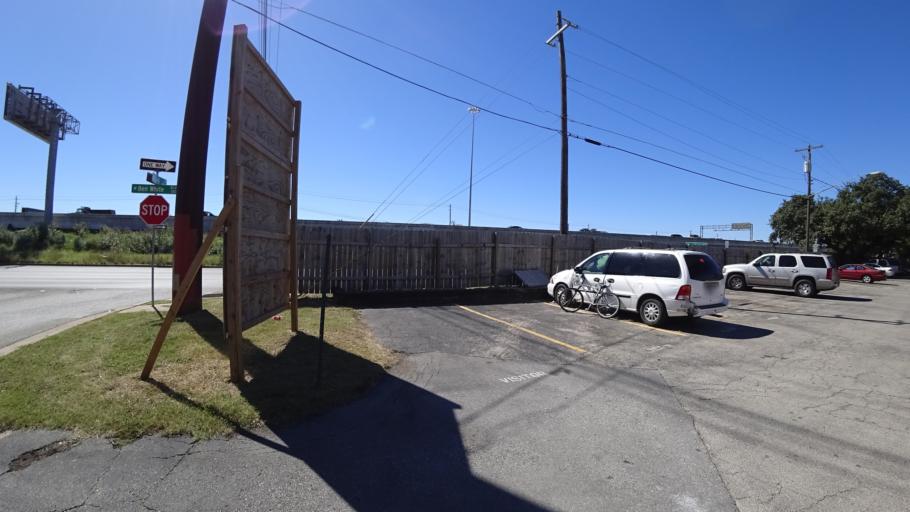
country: US
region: Texas
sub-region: Travis County
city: Rollingwood
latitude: 30.2295
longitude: -97.7857
